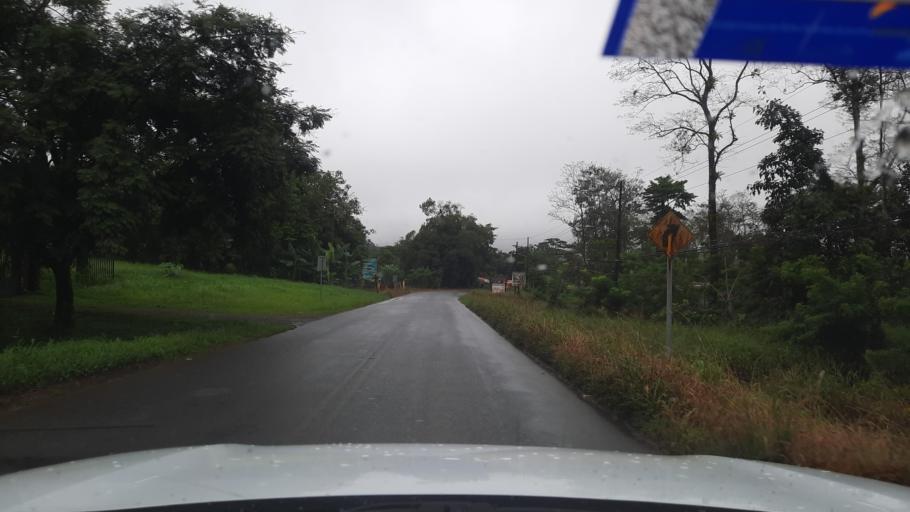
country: CR
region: Alajuela
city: Bijagua
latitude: 10.7288
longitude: -85.0593
